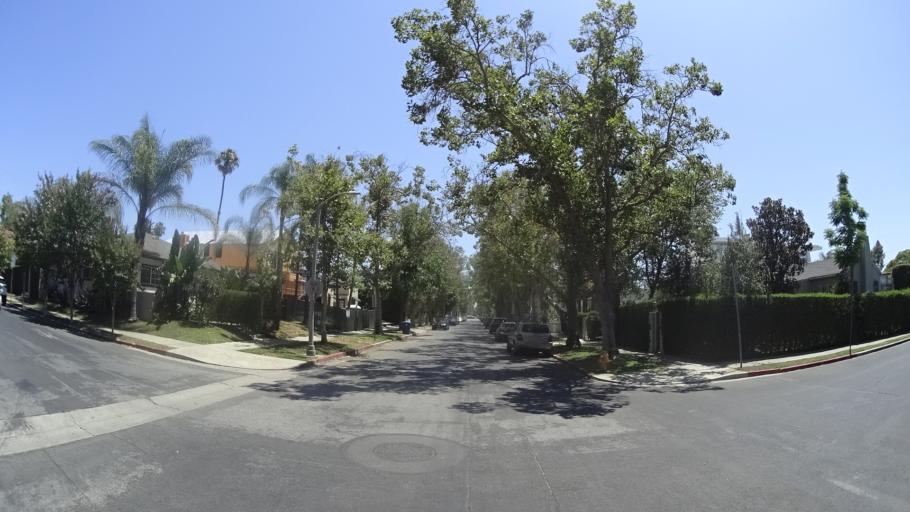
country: US
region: California
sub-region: Los Angeles County
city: Hollywood
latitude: 34.0853
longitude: -118.3416
